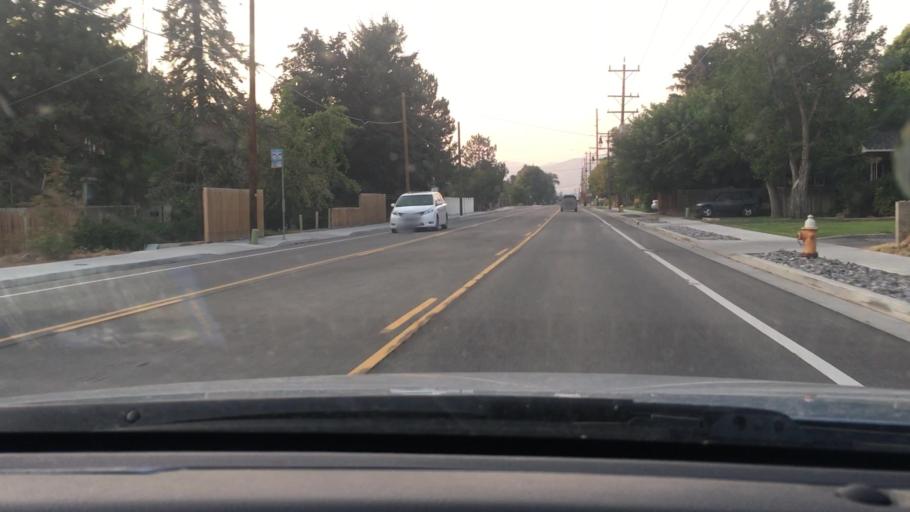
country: US
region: Utah
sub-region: Salt Lake County
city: Canyon Rim
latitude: 40.6921
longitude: -111.8244
